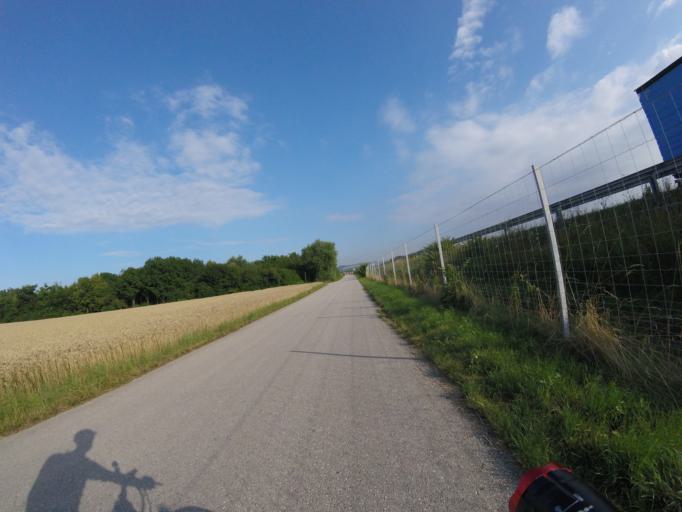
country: AT
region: Lower Austria
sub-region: Politischer Bezirk Baden
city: Trumau
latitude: 48.0213
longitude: 16.3537
